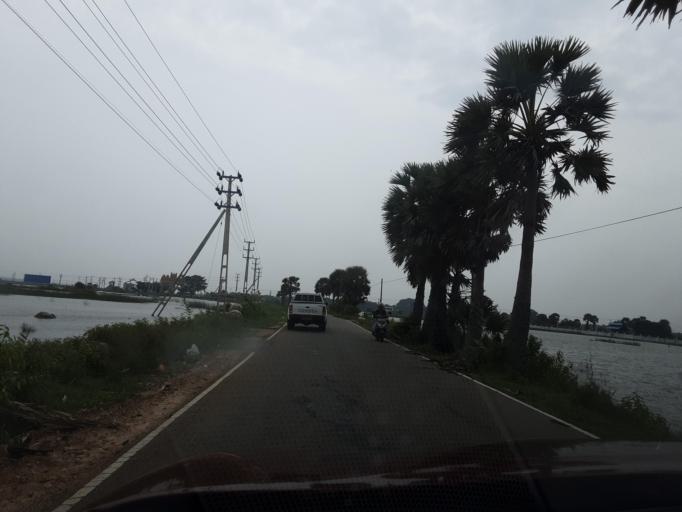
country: LK
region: Northern Province
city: Jaffna
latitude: 9.6649
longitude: 80.0590
